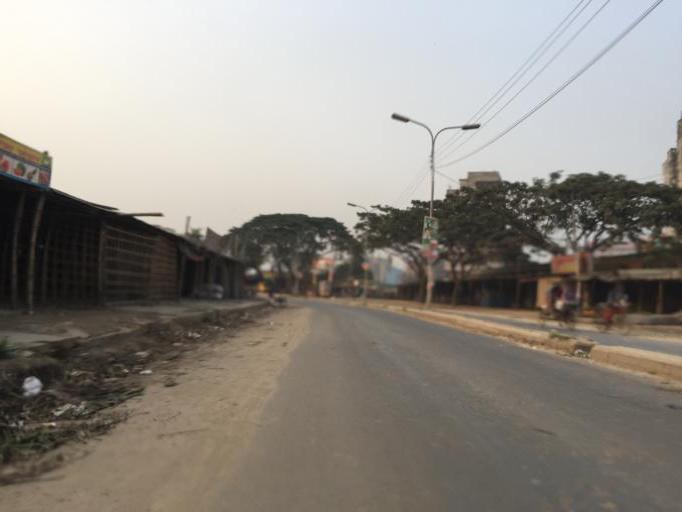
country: BD
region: Dhaka
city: Azimpur
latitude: 23.7974
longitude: 90.3470
